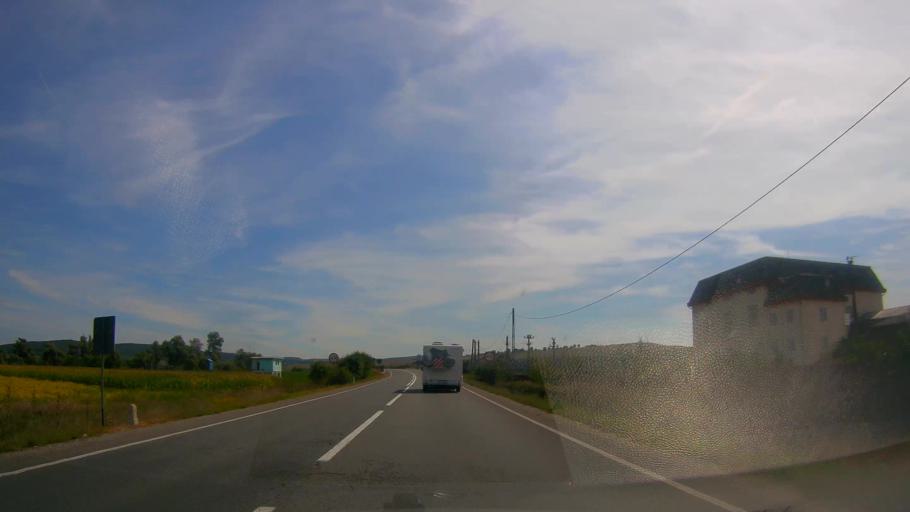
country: RO
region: Mures
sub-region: Comuna Balauseri
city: Balauseri
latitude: 46.4060
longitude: 24.7028
